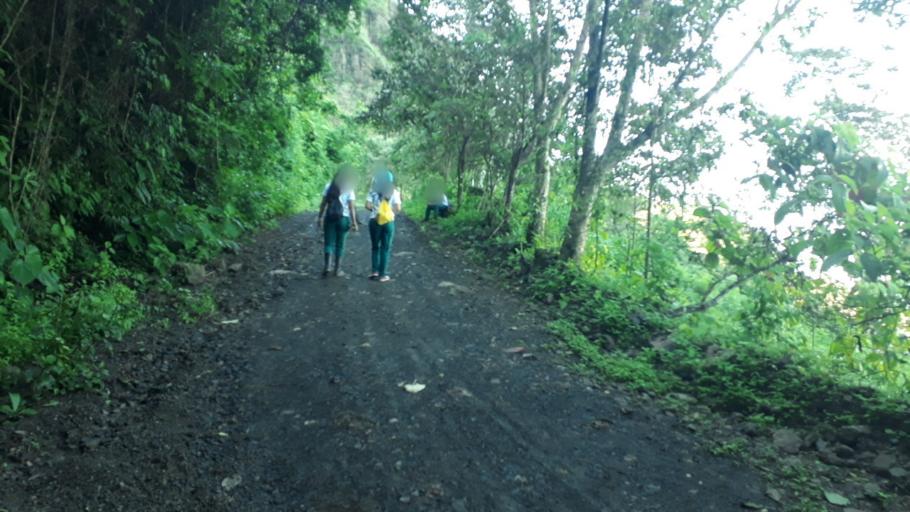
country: CO
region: Casanare
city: Nunchia
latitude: 5.6589
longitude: -72.4217
